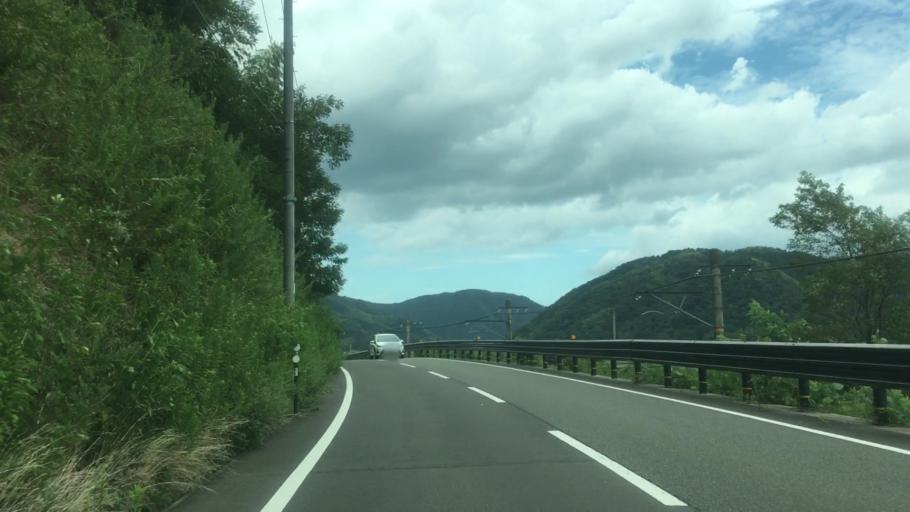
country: JP
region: Hyogo
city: Toyooka
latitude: 35.5741
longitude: 134.8049
